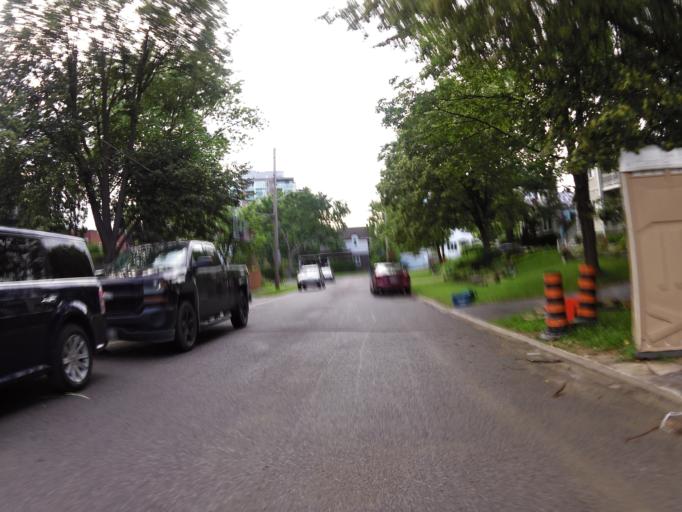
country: CA
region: Ontario
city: Ottawa
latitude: 45.3885
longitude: -75.7565
